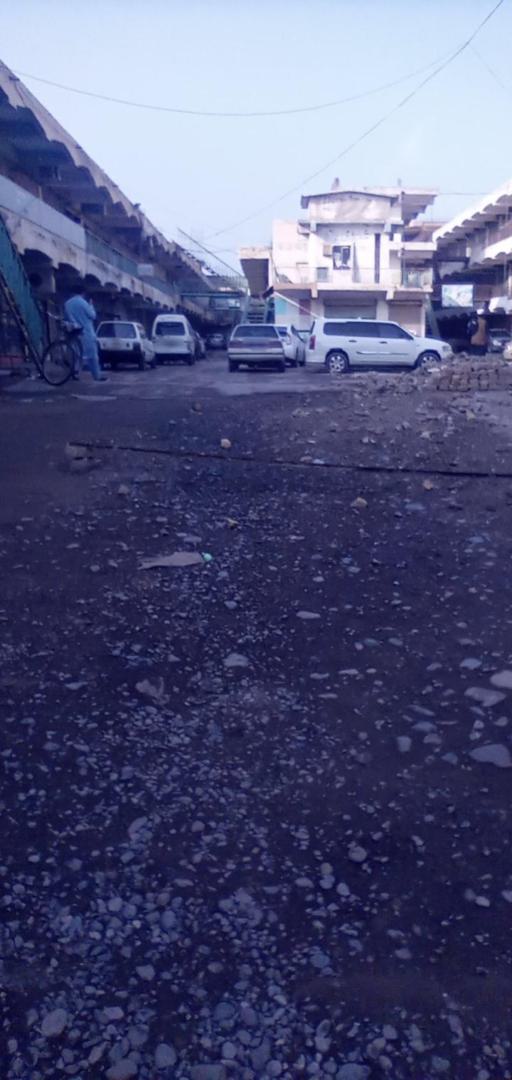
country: PK
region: Khyber Pakhtunkhwa
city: Peshawar
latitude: 33.9993
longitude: 71.4244
